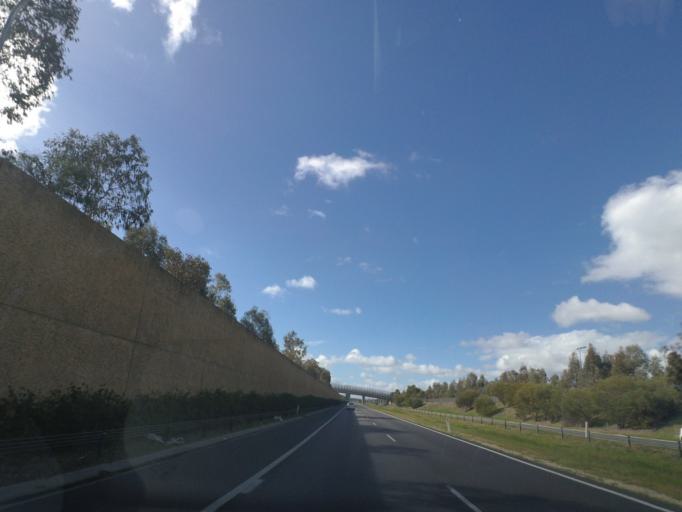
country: AU
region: New South Wales
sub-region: Albury Municipality
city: Albury
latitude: -36.0712
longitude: 146.9322
